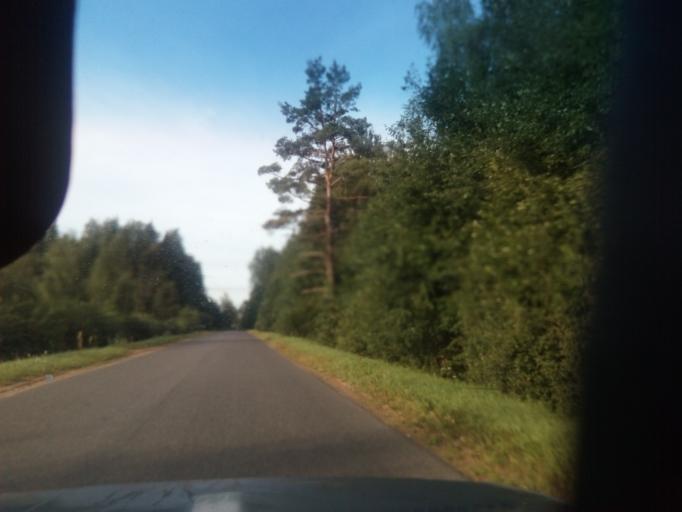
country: BY
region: Vitebsk
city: Dzisna
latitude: 55.6448
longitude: 28.3183
